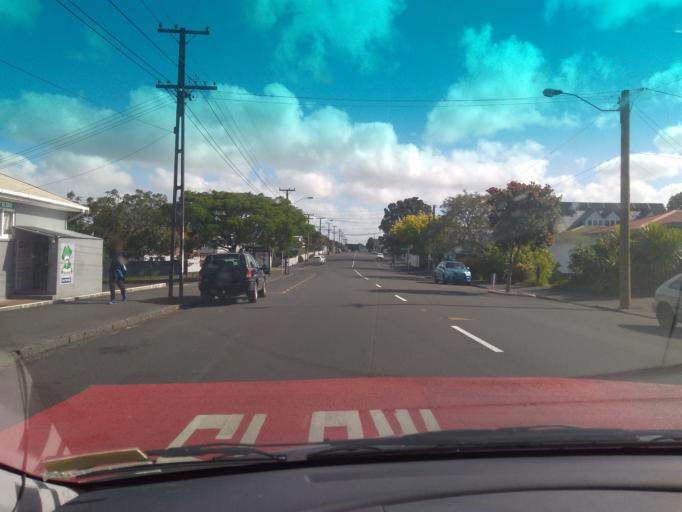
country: NZ
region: Auckland
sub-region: Auckland
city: Rosebank
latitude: -36.8564
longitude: 174.7035
